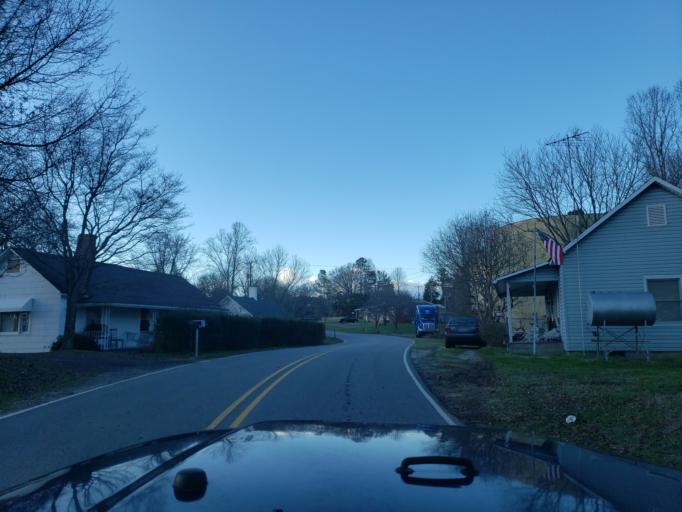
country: US
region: North Carolina
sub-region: Cleveland County
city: Shelby
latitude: 35.4141
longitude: -81.5654
